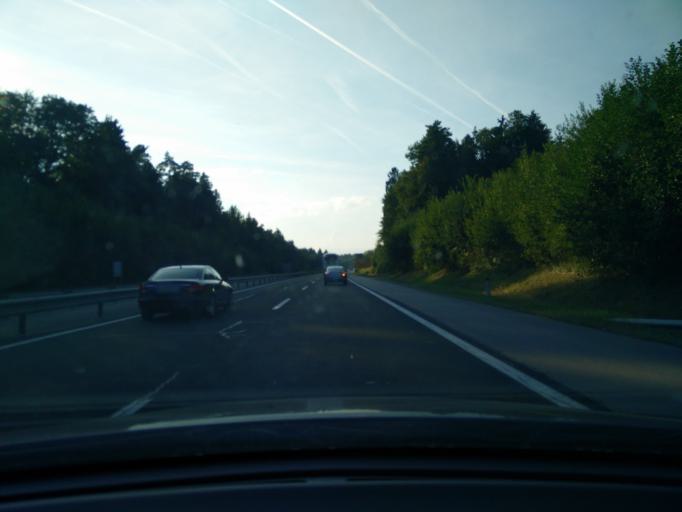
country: SI
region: Kranj
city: Kokrica
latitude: 46.2642
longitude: 14.3457
